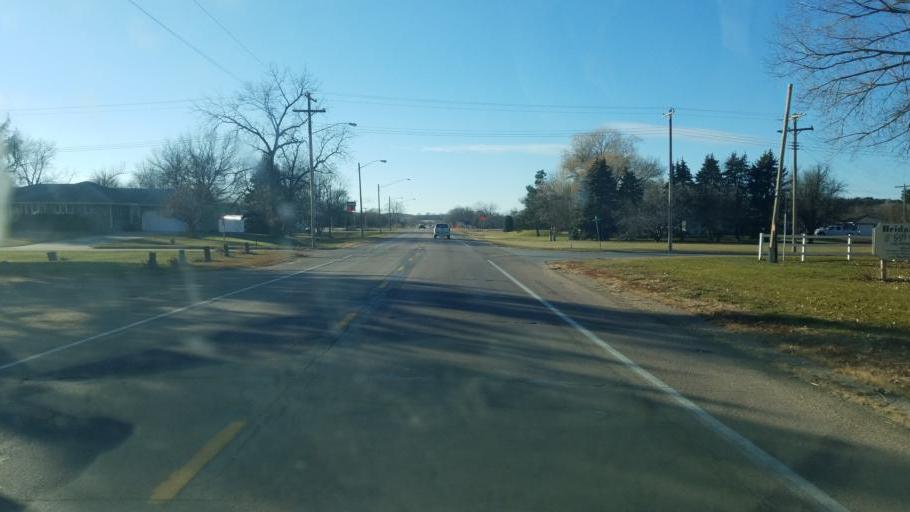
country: US
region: South Dakota
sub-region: Union County
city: Dakota Dunes
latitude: 42.4483
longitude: -96.5686
